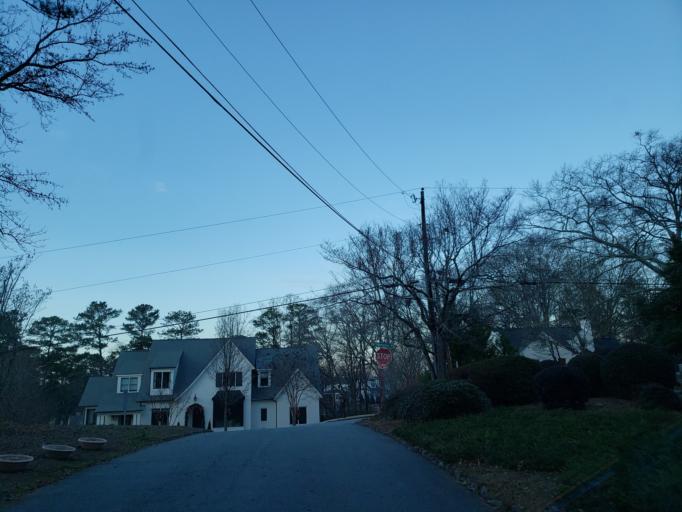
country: US
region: Georgia
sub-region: Fulton County
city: Roswell
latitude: 34.0305
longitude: -84.3645
